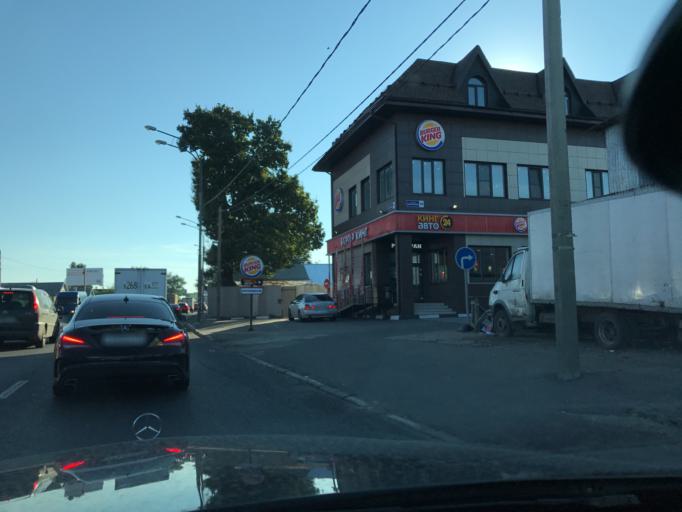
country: RU
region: Moscow
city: Vostochnyy
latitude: 55.8177
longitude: 37.8505
